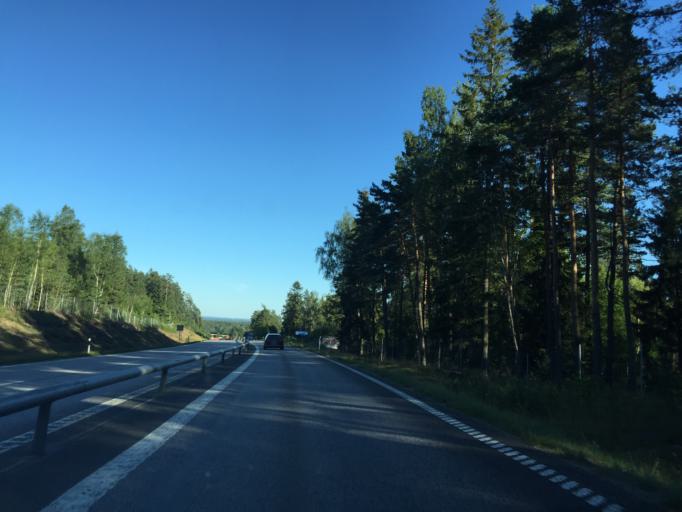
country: SE
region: OErebro
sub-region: Lekebergs Kommun
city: Fjugesta
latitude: 59.2555
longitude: 14.8156
